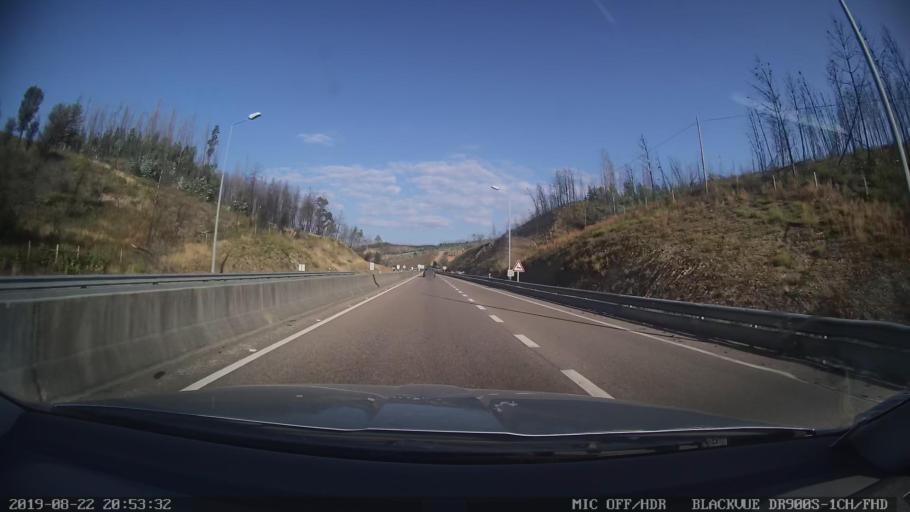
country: PT
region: Castelo Branco
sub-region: Proenca-A-Nova
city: Proenca-a-Nova
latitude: 39.7712
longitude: -7.9942
